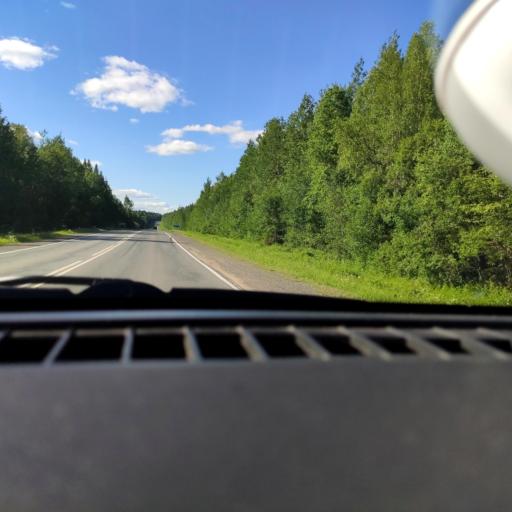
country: RU
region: Perm
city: Perm
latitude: 58.1580
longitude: 56.2487
